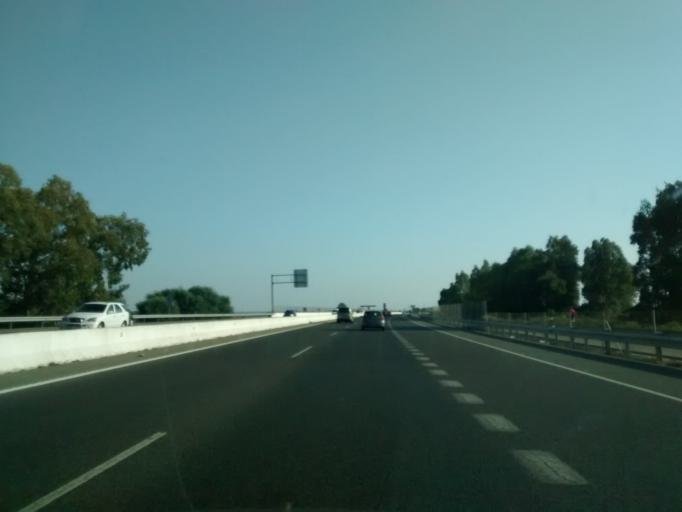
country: ES
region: Andalusia
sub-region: Provincia de Cadiz
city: San Fernando
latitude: 36.4938
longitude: -6.1437
